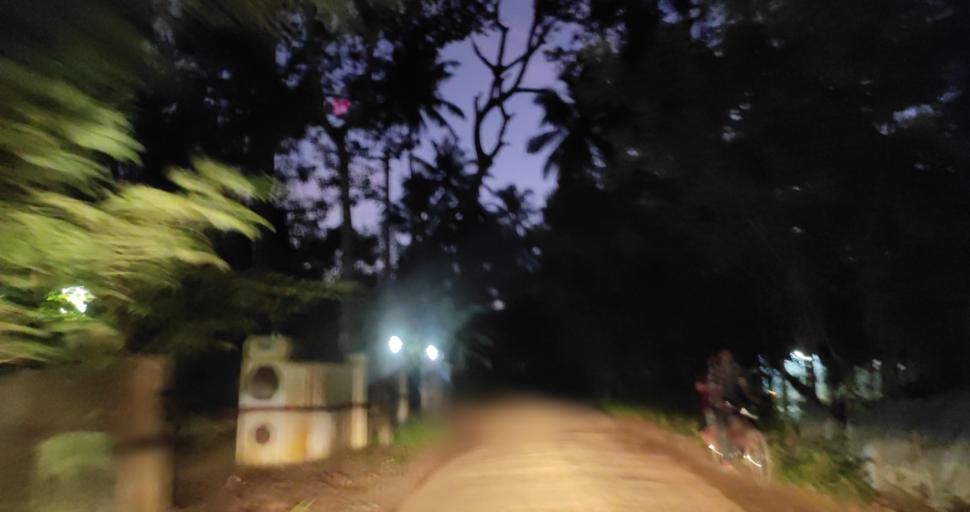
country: IN
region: Kerala
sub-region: Alappuzha
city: Shertallai
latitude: 9.6236
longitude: 76.3485
